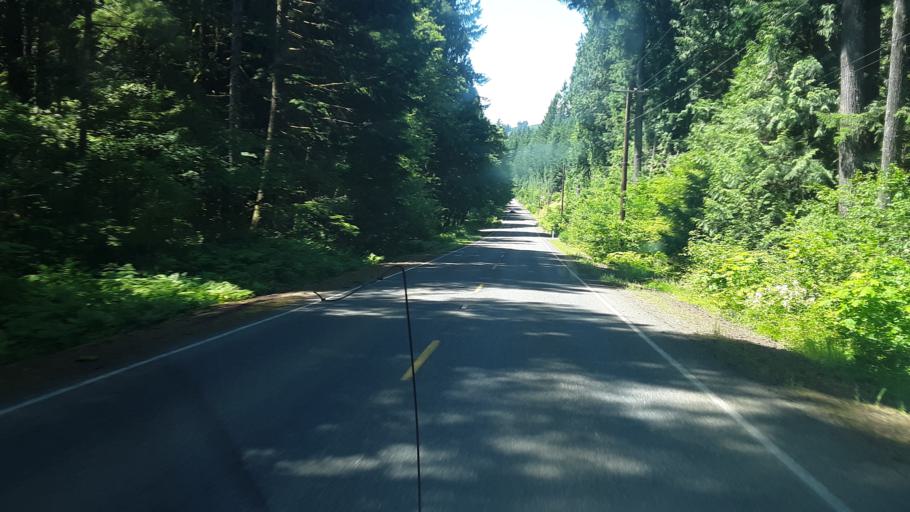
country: US
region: Washington
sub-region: Clark County
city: Amboy
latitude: 46.0575
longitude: -122.2922
